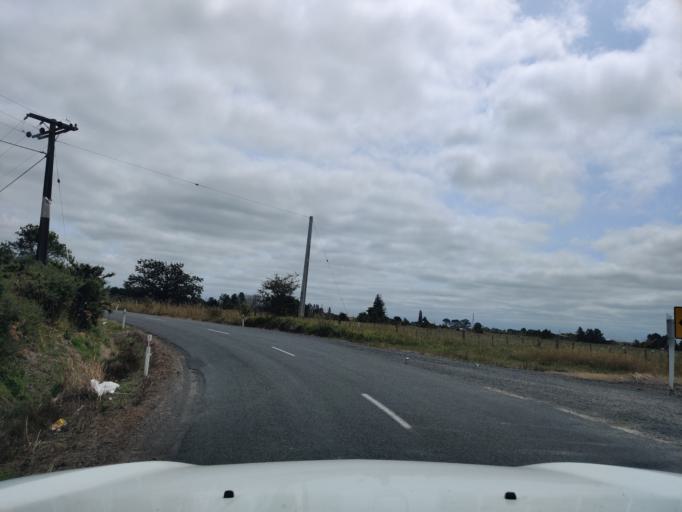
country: NZ
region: Waikato
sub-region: Waikato District
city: Te Kauwhata
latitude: -37.5257
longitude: 175.1691
